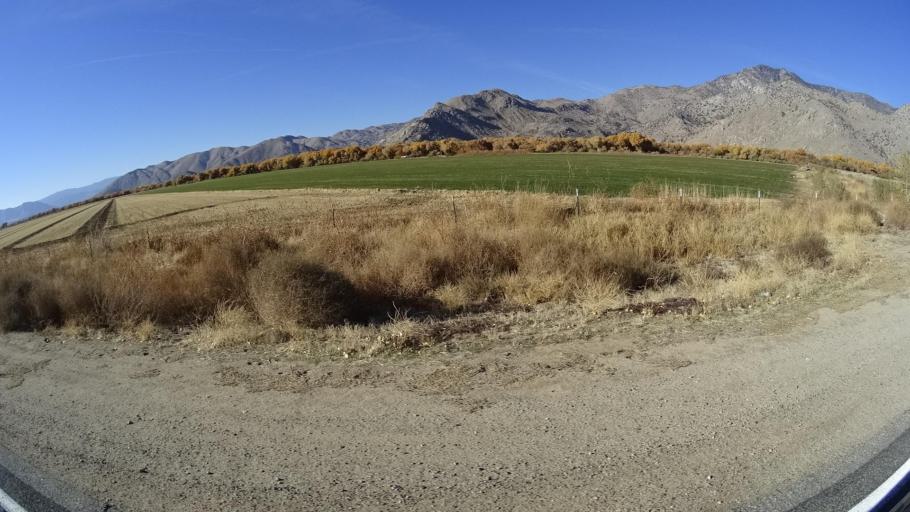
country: US
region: California
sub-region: Kern County
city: Weldon
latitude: 35.6769
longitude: -118.2547
